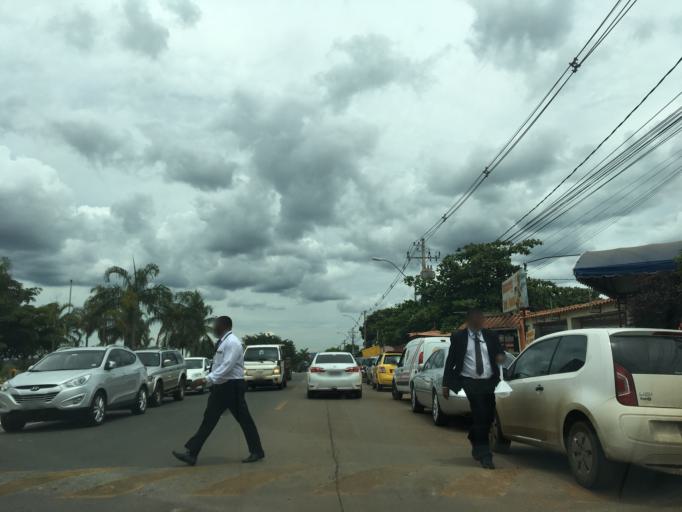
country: BR
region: Federal District
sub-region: Brasilia
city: Brasilia
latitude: -15.7958
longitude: -47.8533
